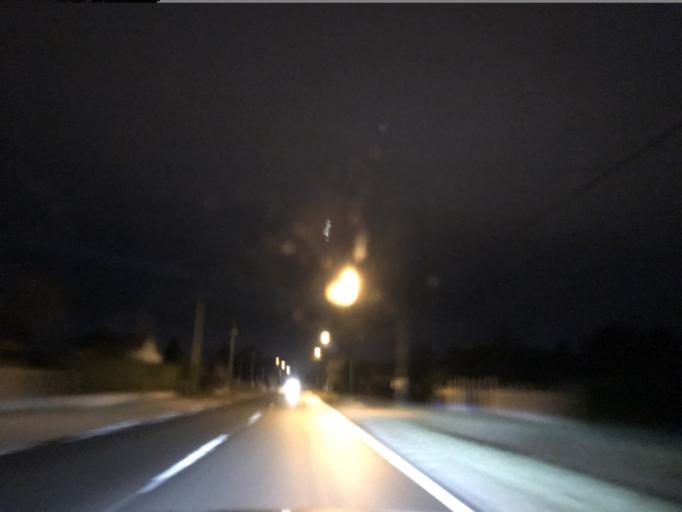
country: FR
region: Auvergne
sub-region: Departement de l'Allier
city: Abrest
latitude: 46.0989
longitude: 3.4299
